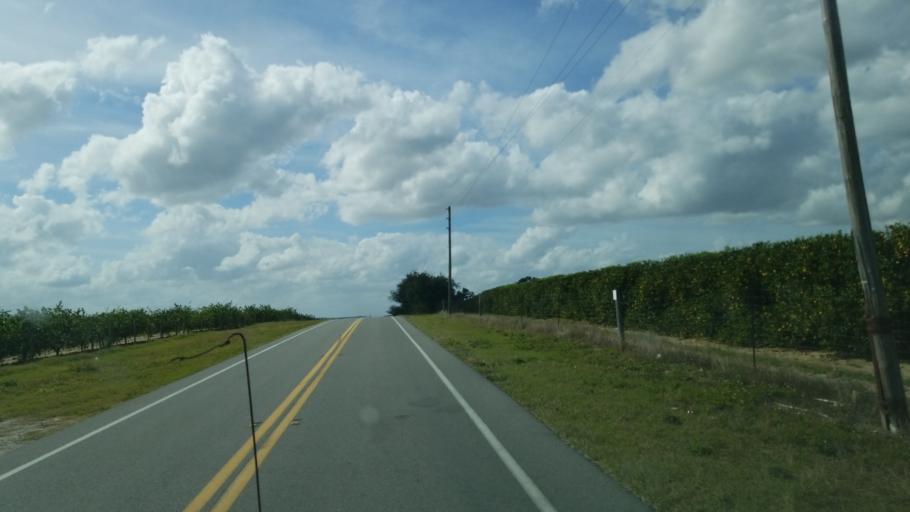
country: US
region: Florida
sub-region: Polk County
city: Babson Park
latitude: 27.9253
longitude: -81.4719
